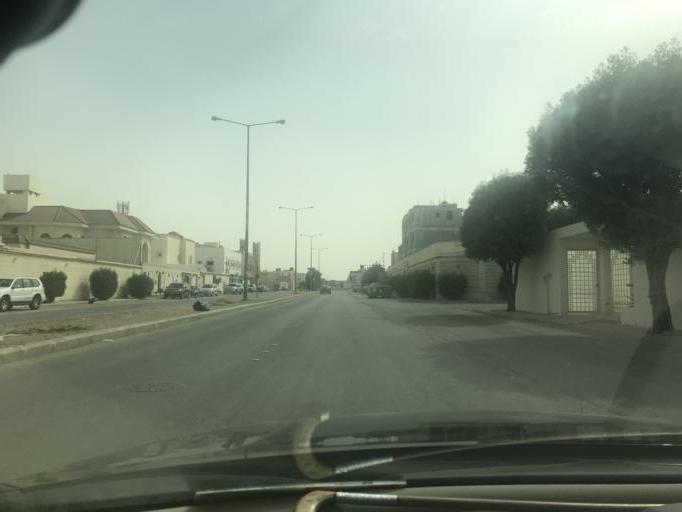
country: SA
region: Ar Riyad
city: Riyadh
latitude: 24.7384
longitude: 46.7909
